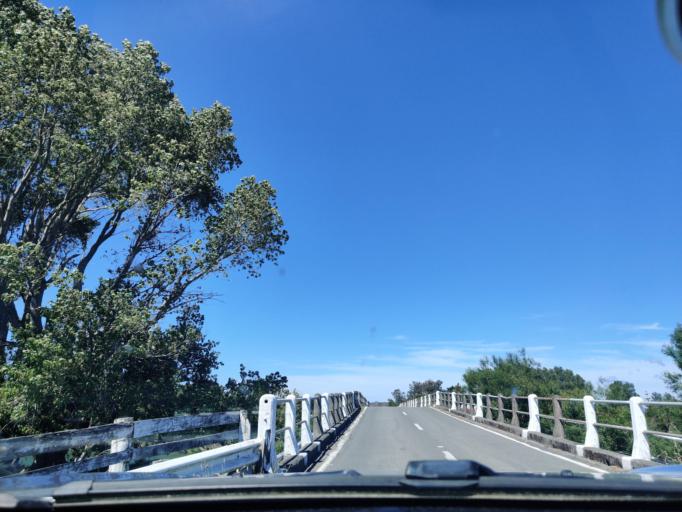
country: NZ
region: Wellington
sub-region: Upper Hutt City
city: Upper Hutt
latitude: -41.2863
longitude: 175.2690
